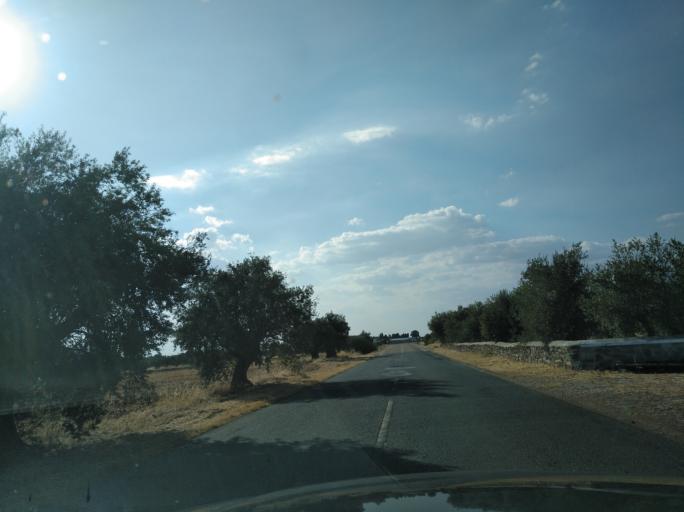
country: PT
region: Evora
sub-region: Mourao
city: Mourao
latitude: 38.3772
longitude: -7.3282
